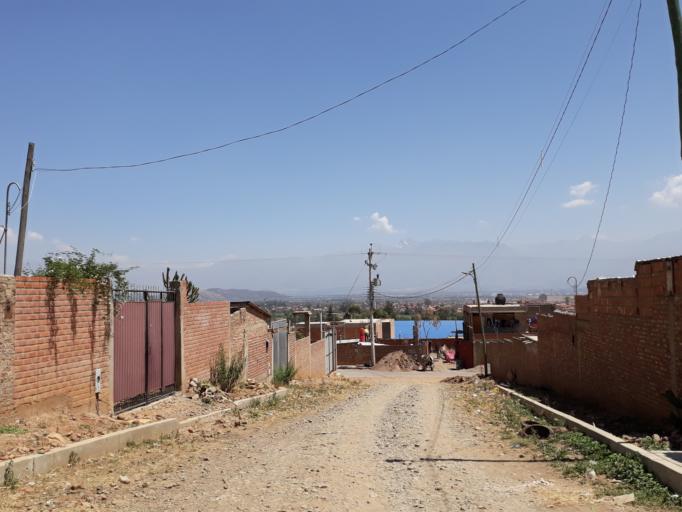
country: BO
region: Cochabamba
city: Cochabamba
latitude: -17.4626
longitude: -66.1359
